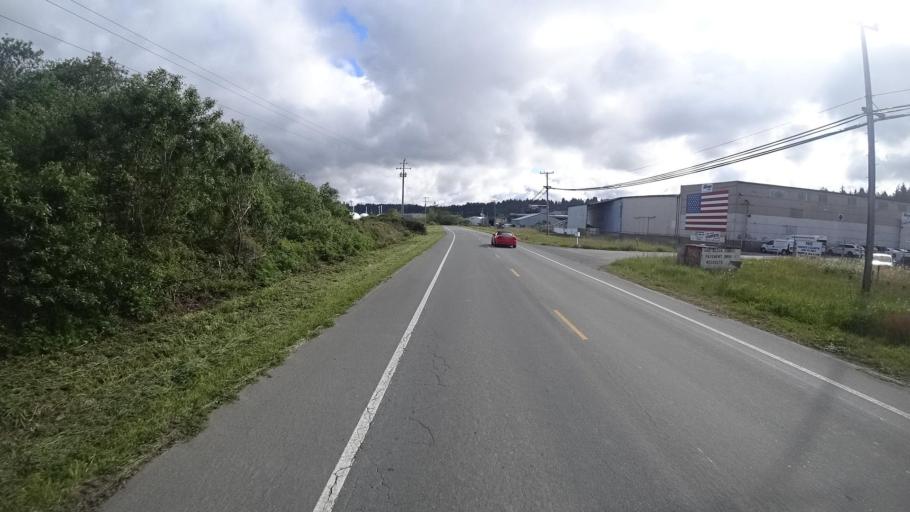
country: US
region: California
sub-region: Humboldt County
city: Arcata
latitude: 40.8954
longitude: -124.0775
